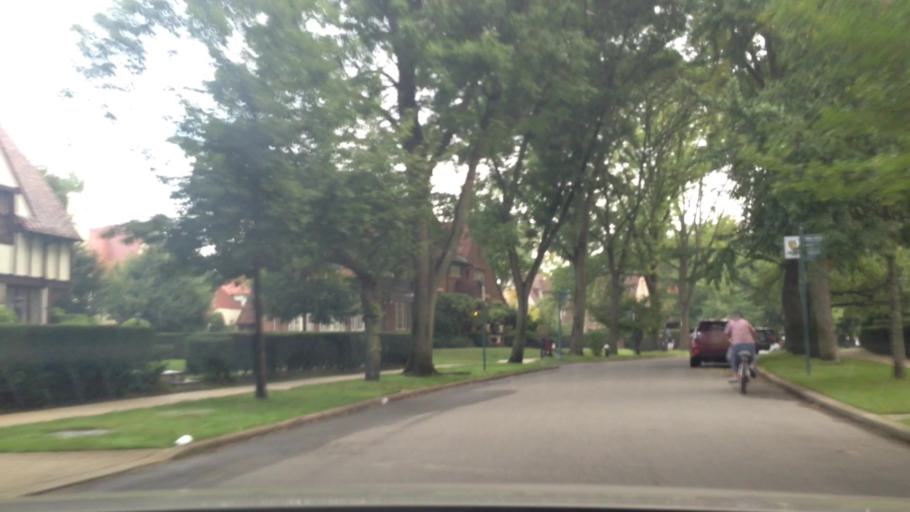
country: US
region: New York
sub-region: Queens County
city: Borough of Queens
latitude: 40.7153
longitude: -73.8448
